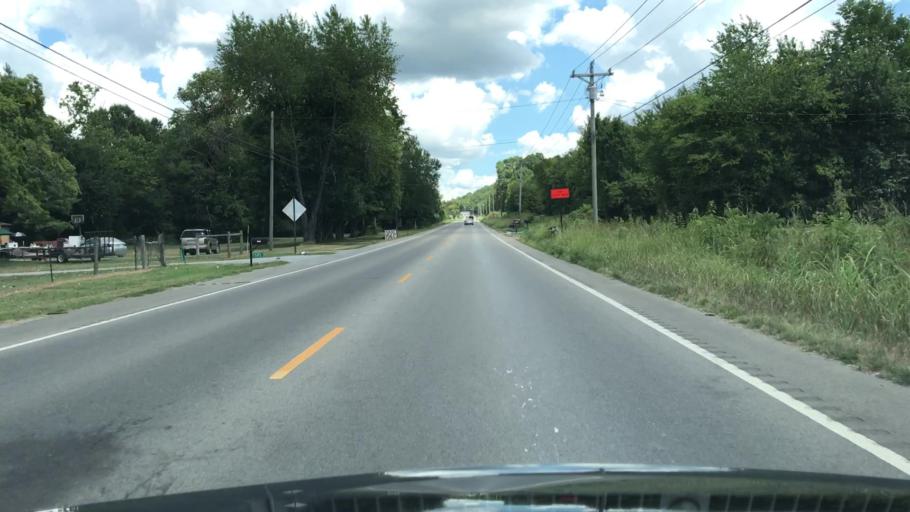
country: US
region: Tennessee
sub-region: Williamson County
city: Nolensville
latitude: 35.9114
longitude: -86.6616
